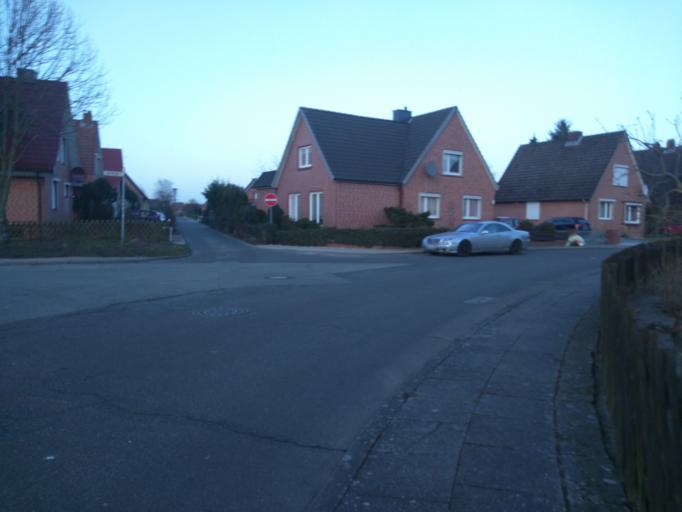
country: DE
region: Schleswig-Holstein
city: Lauenburg
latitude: 53.3767
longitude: 10.5396
